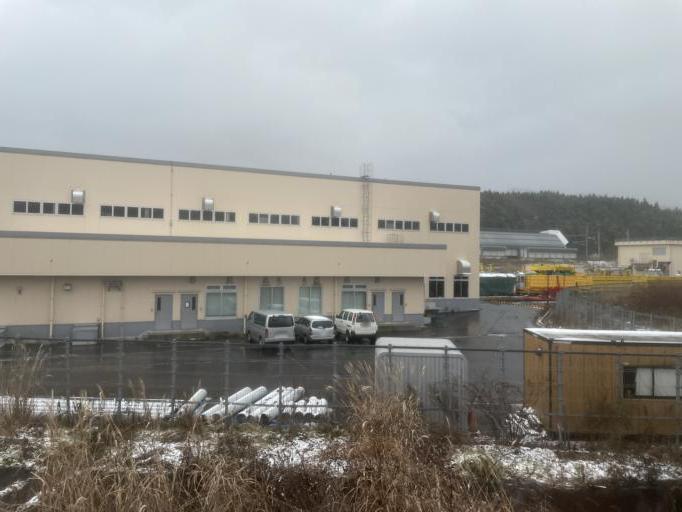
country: JP
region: Aomori
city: Goshogawara
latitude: 41.1409
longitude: 140.5173
